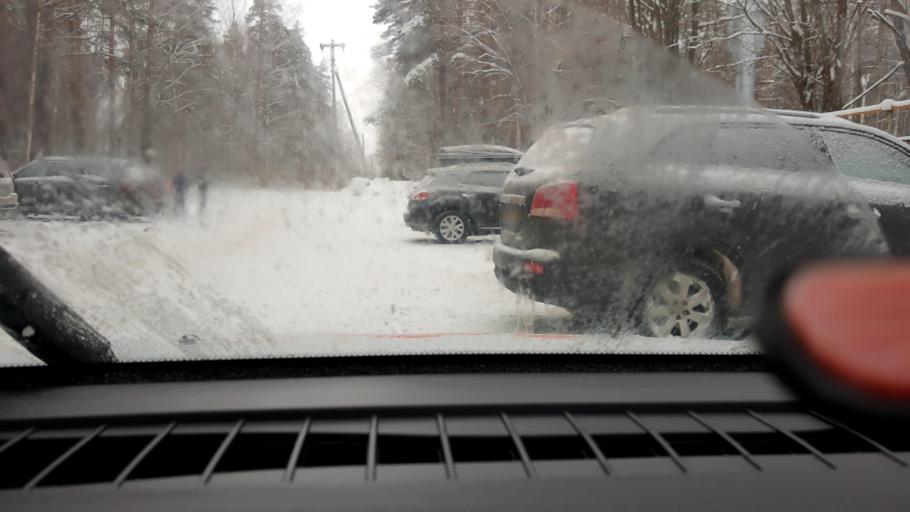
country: RU
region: Nizjnij Novgorod
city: Pamyat' Parizhskoy Kommuny
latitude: 56.0653
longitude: 44.4874
